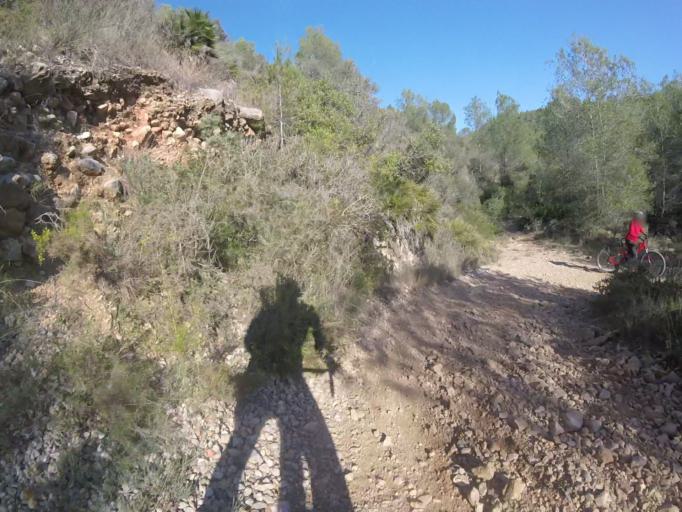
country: ES
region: Valencia
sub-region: Provincia de Castello
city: Santa Magdalena de Pulpis
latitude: 40.3117
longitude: 0.3338
